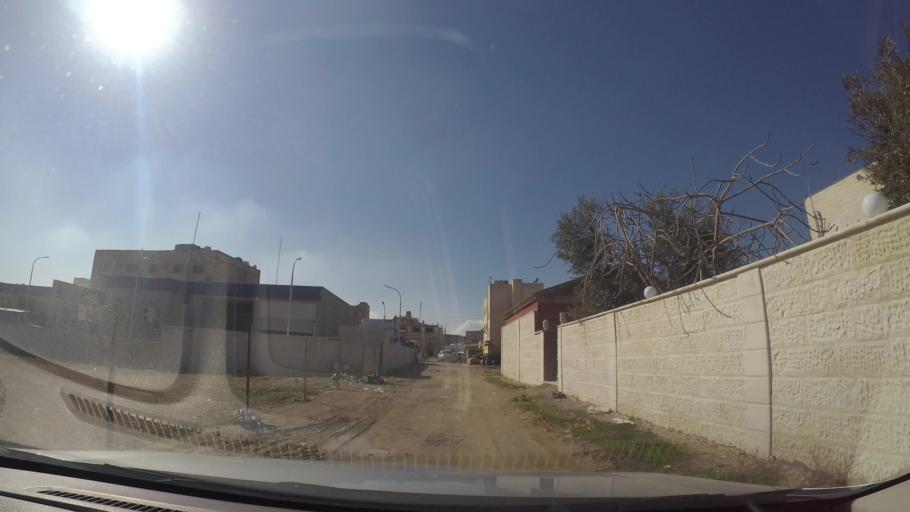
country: JO
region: Amman
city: Al Bunayyat ash Shamaliyah
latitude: 31.9028
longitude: 35.8920
